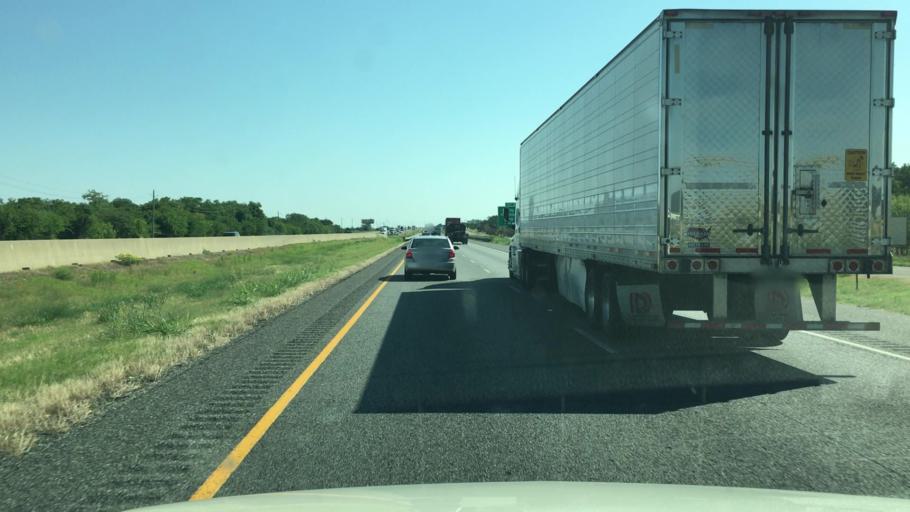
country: US
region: Texas
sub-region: Hunt County
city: Greenville
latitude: 33.0709
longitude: -96.1458
